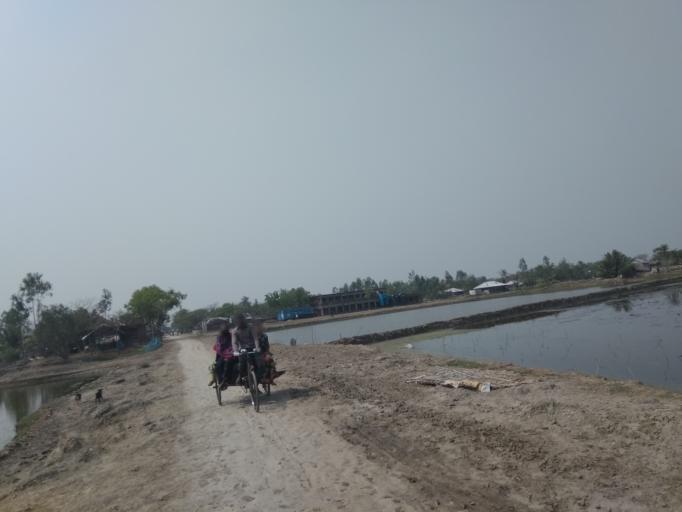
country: IN
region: West Bengal
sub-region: North 24 Parganas
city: Taki
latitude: 22.3480
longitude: 89.2211
